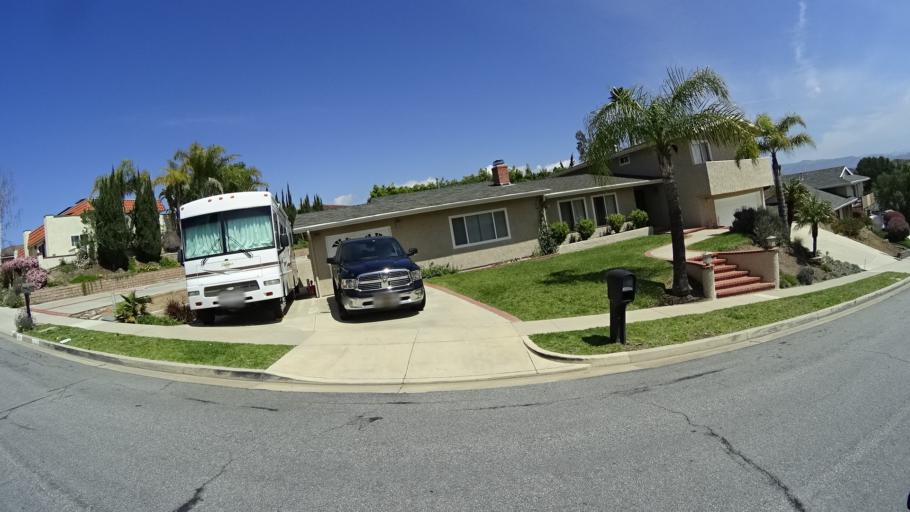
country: US
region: California
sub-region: Ventura County
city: Moorpark
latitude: 34.2393
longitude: -118.8531
